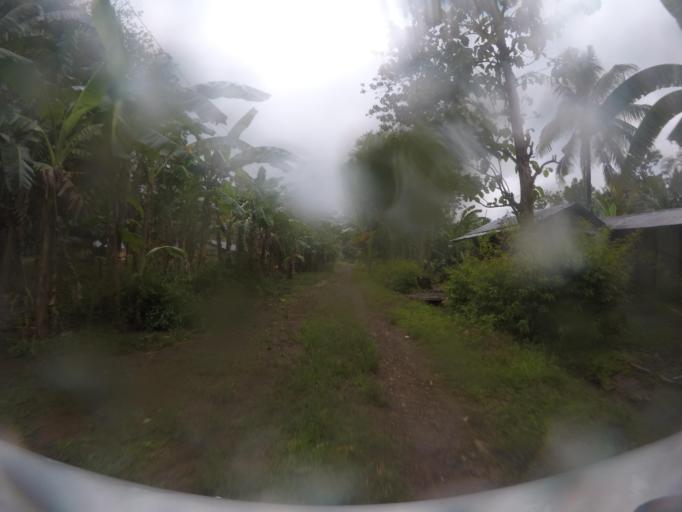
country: TL
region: Bobonaro
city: Maliana
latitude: -8.9636
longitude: 125.2149
